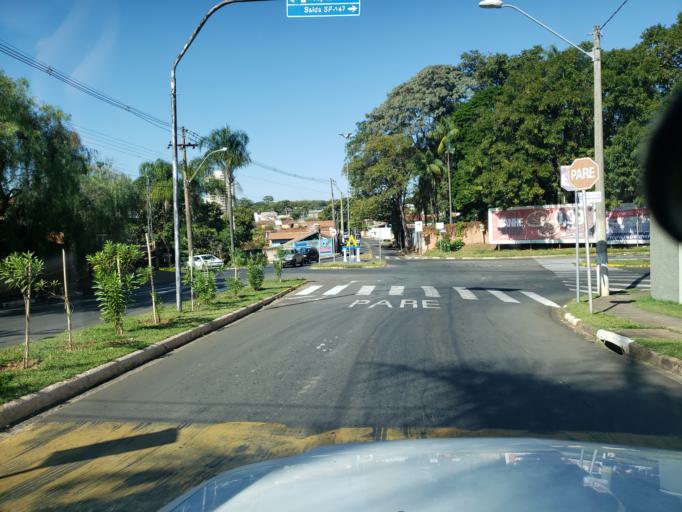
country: BR
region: Sao Paulo
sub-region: Itapira
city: Itapira
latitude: -22.4289
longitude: -46.8362
